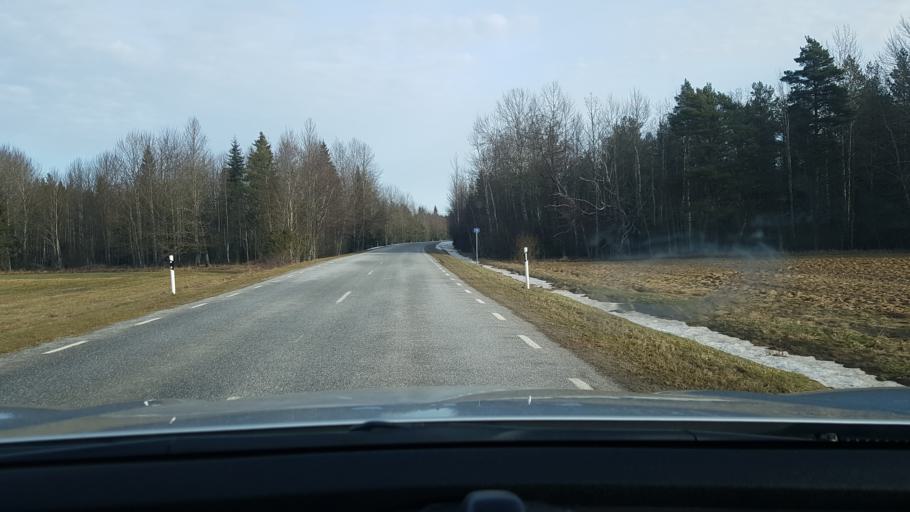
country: EE
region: Saare
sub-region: Kuressaare linn
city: Kuressaare
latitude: 58.4186
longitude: 22.6634
